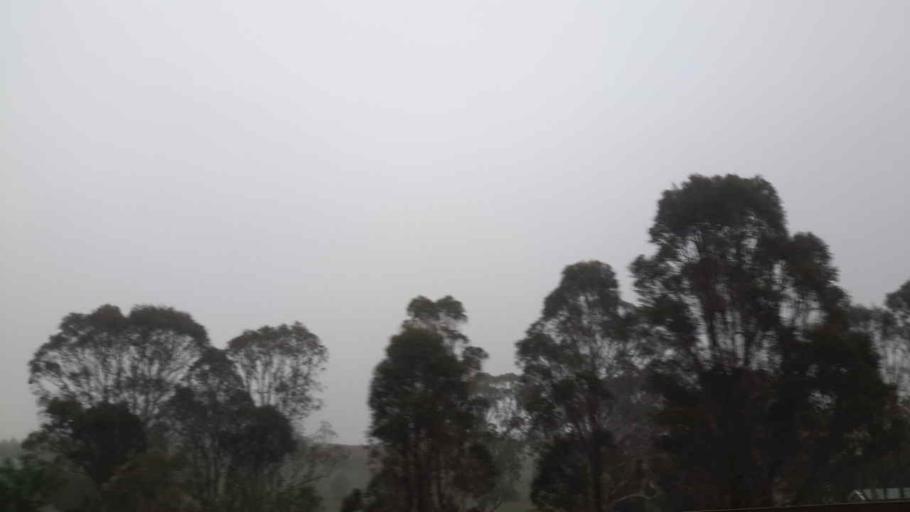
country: AU
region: New South Wales
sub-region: Wollondilly
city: Douglas Park
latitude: -34.1545
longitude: 150.7221
